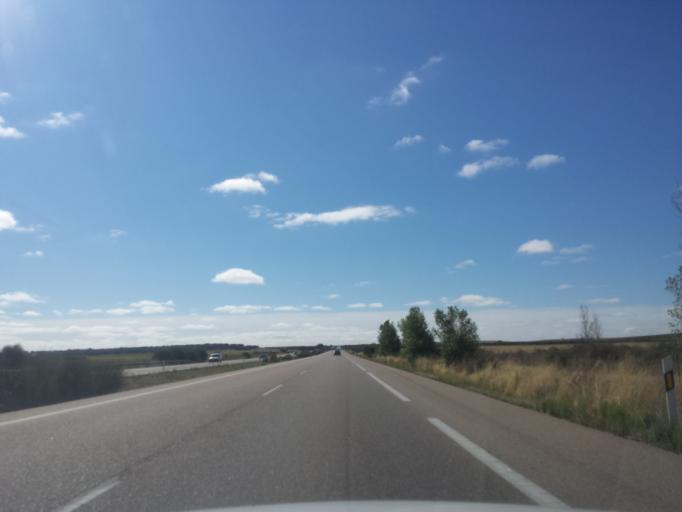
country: ES
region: Castille and Leon
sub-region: Provincia de Zamora
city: Villalpando
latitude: 41.8414
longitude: -5.3937
